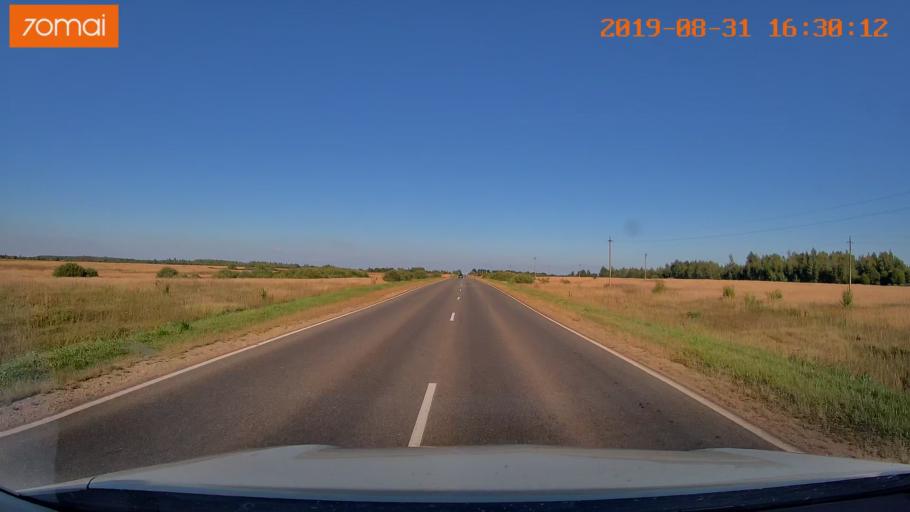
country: RU
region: Kaluga
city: Babynino
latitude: 54.5093
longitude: 35.8246
